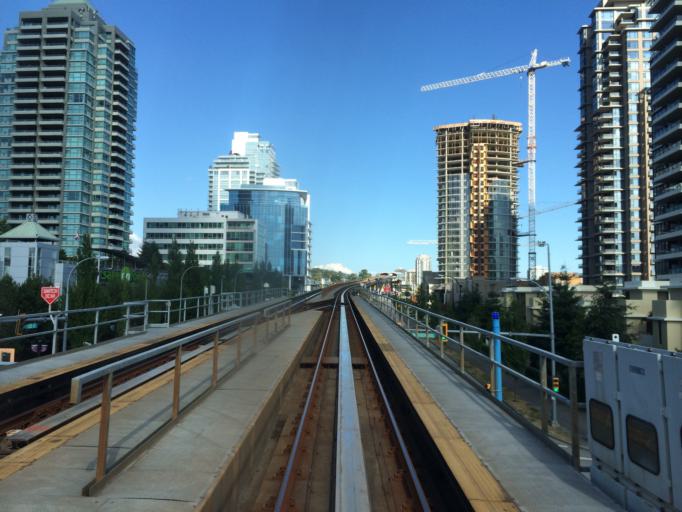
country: CA
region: British Columbia
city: Burnaby
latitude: 49.2664
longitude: -123.0092
